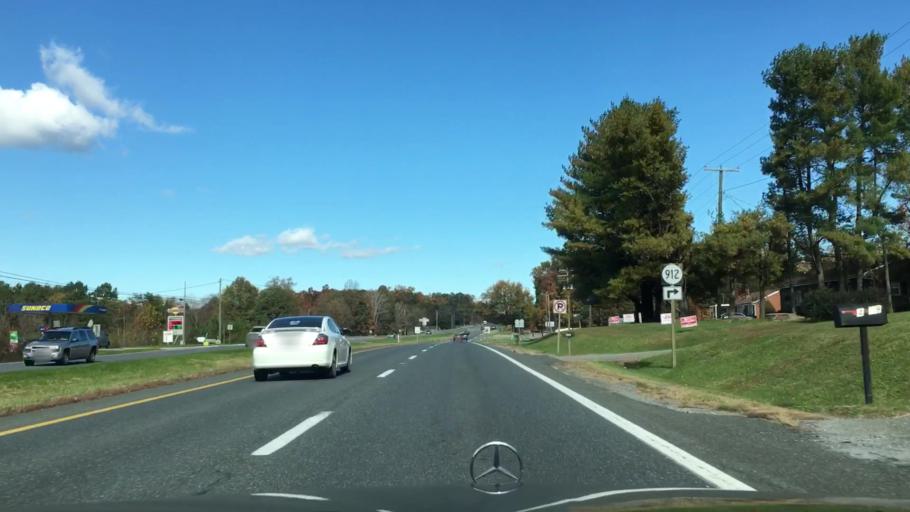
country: US
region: Virginia
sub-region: Campbell County
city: Altavista
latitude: 37.1983
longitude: -79.2034
